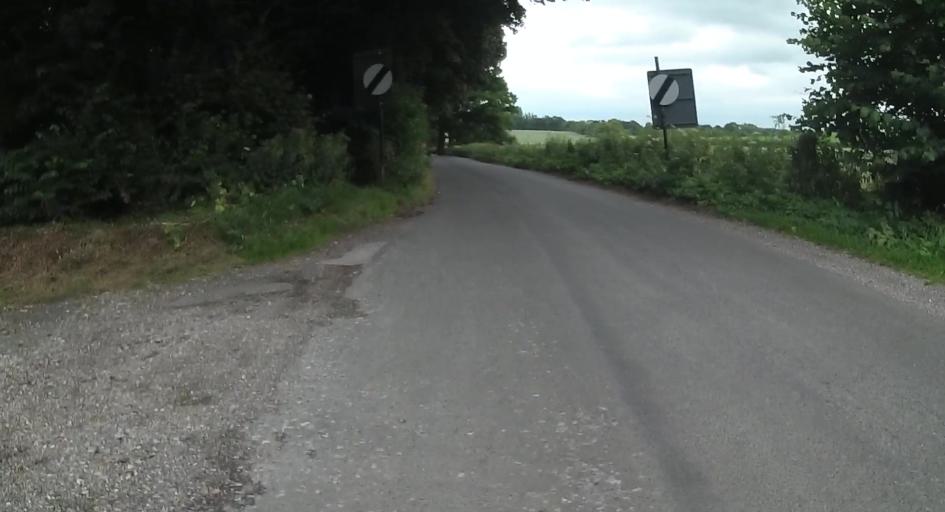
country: GB
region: England
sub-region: Hampshire
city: Swanmore
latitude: 51.0441
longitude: -1.1613
